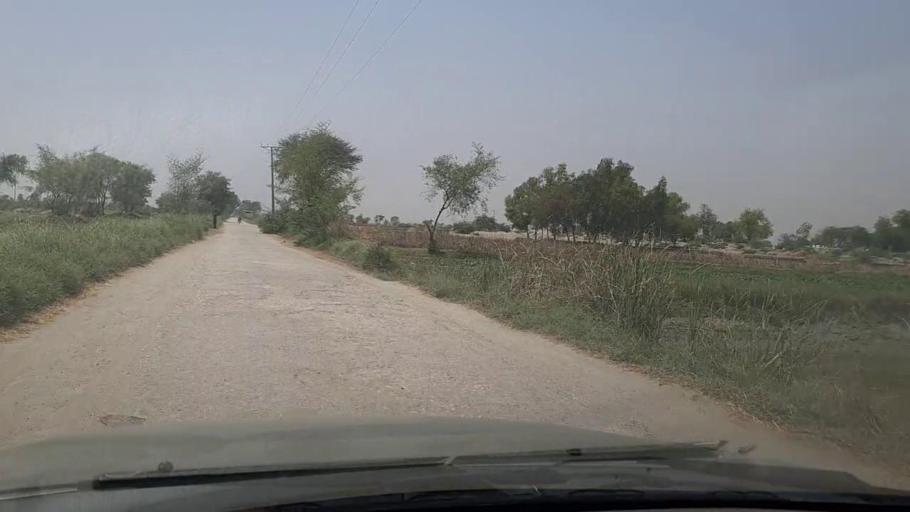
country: PK
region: Sindh
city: Miro Khan
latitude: 27.7628
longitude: 68.1181
